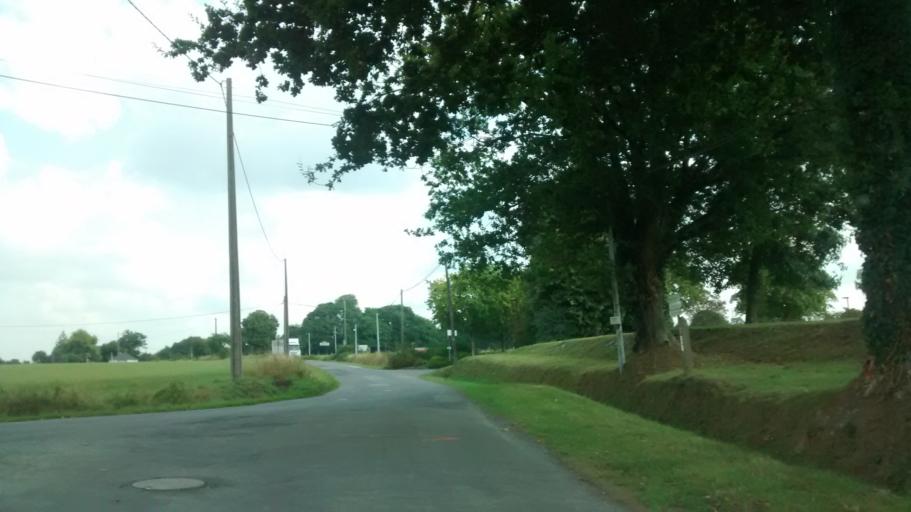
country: FR
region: Brittany
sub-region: Departement d'Ille-et-Vilaine
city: Chatillon-en-Vendelais
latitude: 48.2297
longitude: -1.1792
